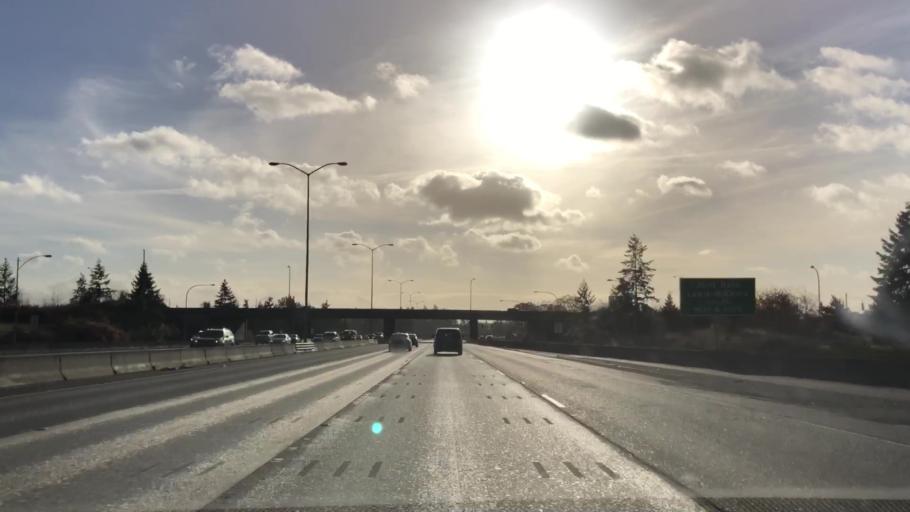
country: US
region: Washington
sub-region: Pierce County
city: McChord Air Force Base
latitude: 47.1645
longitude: -122.4785
